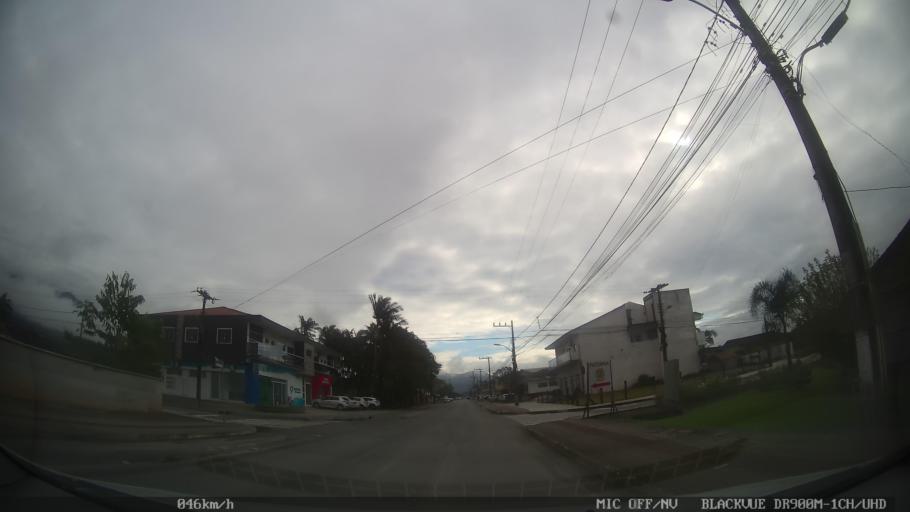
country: BR
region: Santa Catarina
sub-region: Joinville
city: Joinville
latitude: -26.0384
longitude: -48.8566
